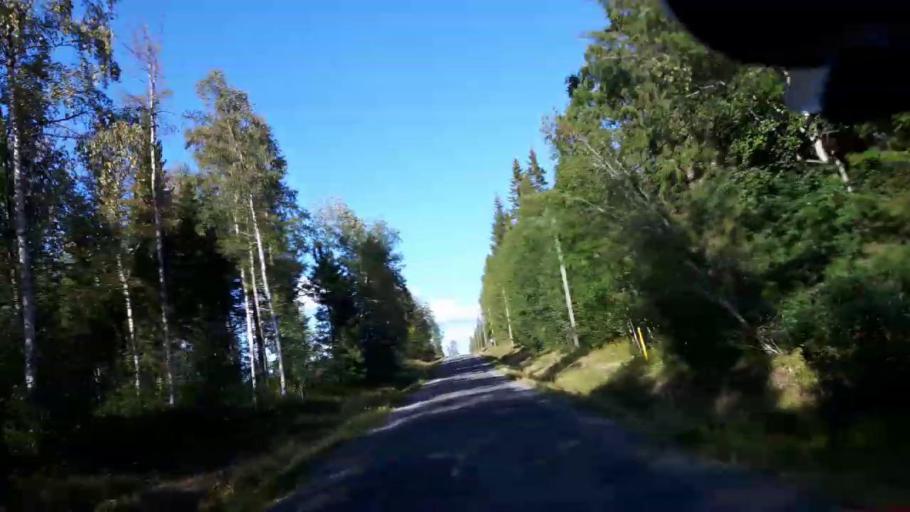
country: SE
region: Jaemtland
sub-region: Ragunda Kommun
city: Hammarstrand
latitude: 63.5033
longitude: 16.0370
